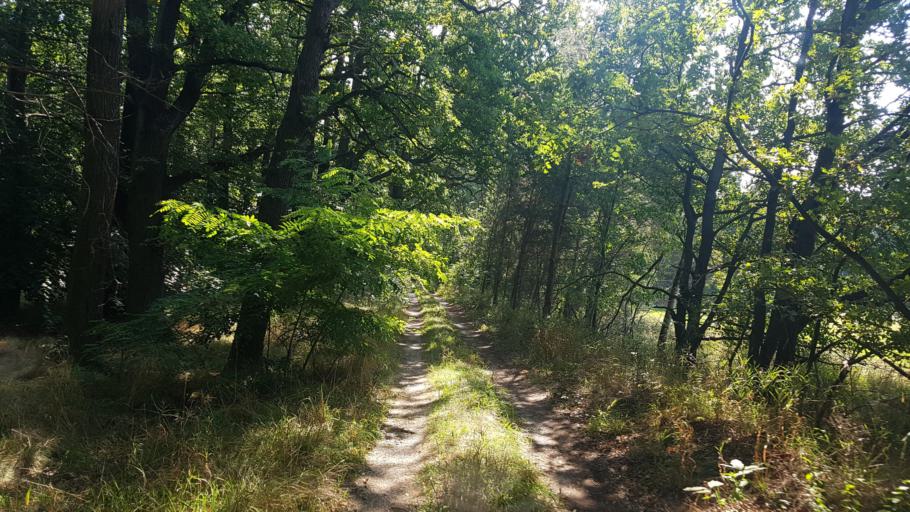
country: DE
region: Brandenburg
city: Calau
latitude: 51.7487
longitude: 13.9898
